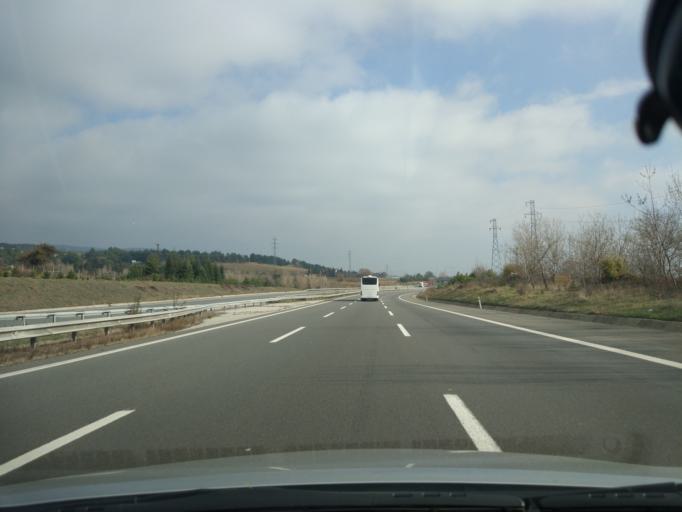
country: TR
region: Bolu
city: Bolu
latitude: 40.7655
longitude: 31.6270
